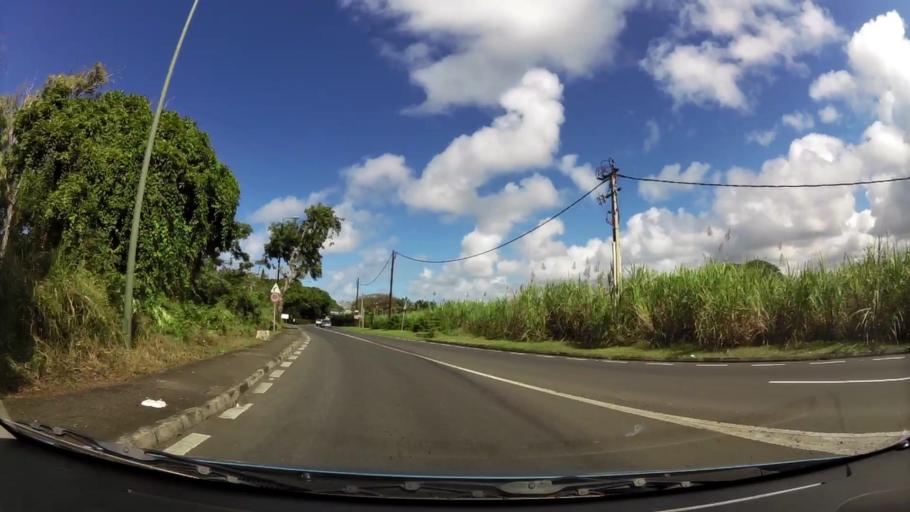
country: MU
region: Grand Port
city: Beau Vallon
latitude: -20.4228
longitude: 57.7016
